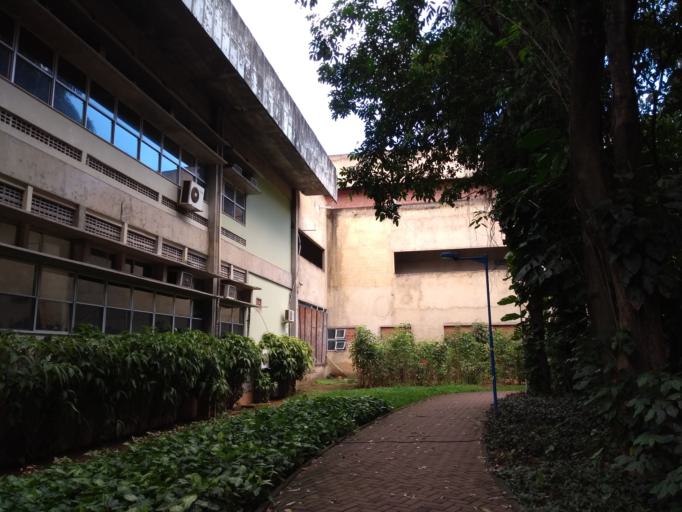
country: BR
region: Bahia
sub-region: Salvador
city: Salvador
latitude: -13.0050
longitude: -38.5100
